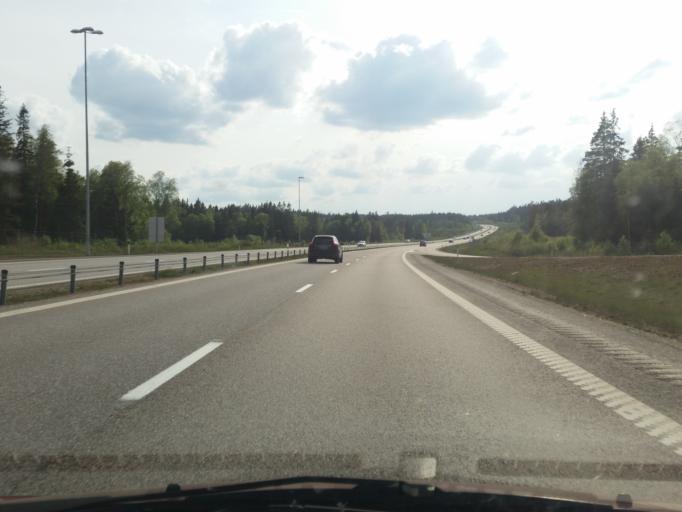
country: SE
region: Vaestra Goetaland
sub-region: Boras Kommun
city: Dalsjofors
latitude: 57.7579
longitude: 13.1009
